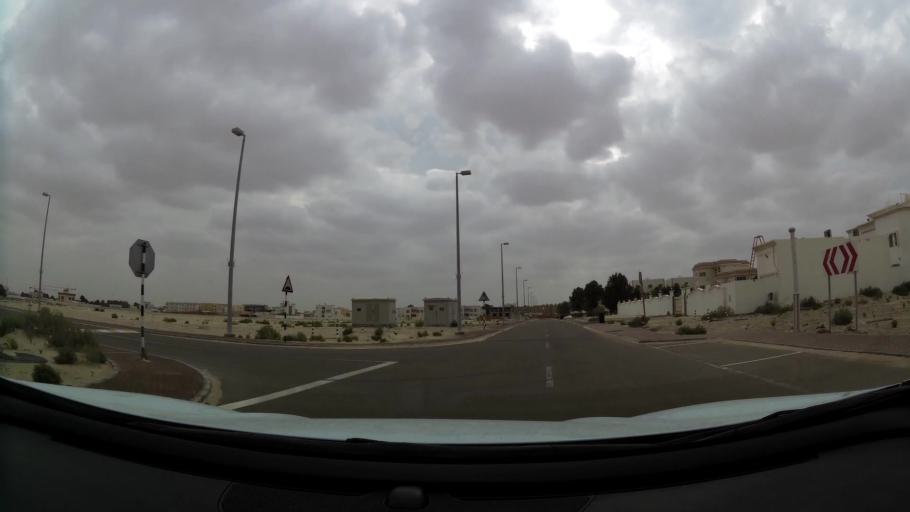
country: AE
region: Abu Dhabi
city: Abu Dhabi
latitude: 24.3799
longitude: 54.6347
